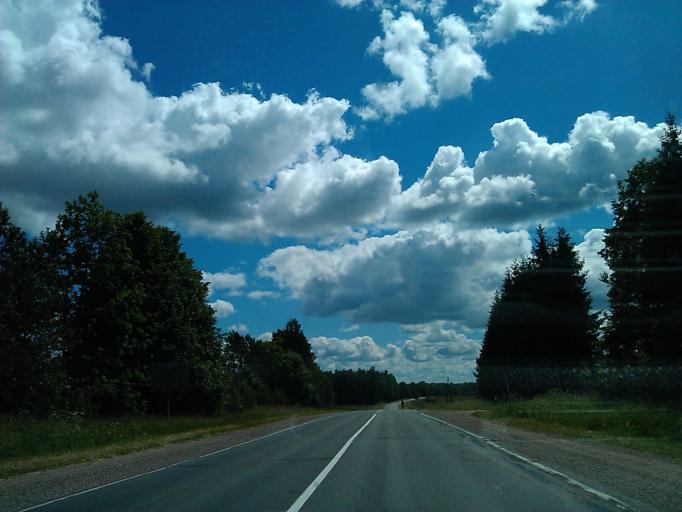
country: LV
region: Vilanu
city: Vilani
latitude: 56.5758
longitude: 26.9070
